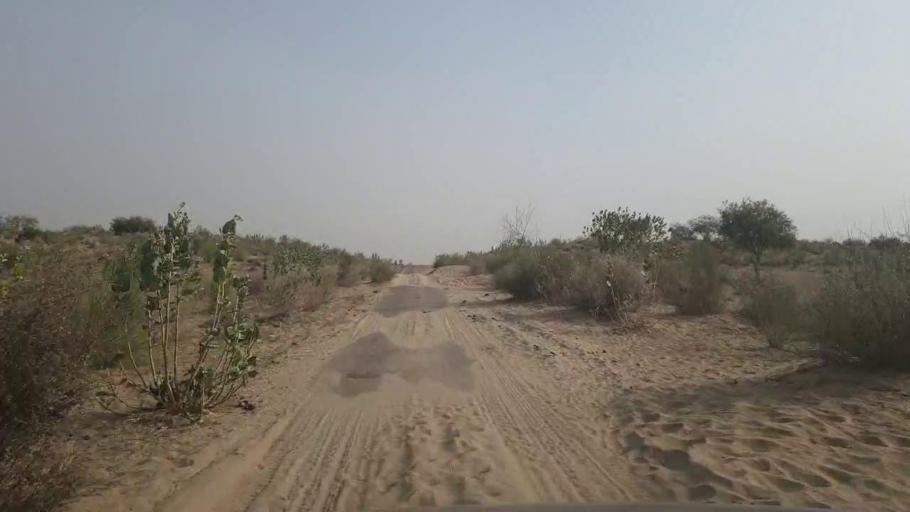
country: PK
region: Sindh
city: Chor
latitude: 25.5102
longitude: 69.9675
